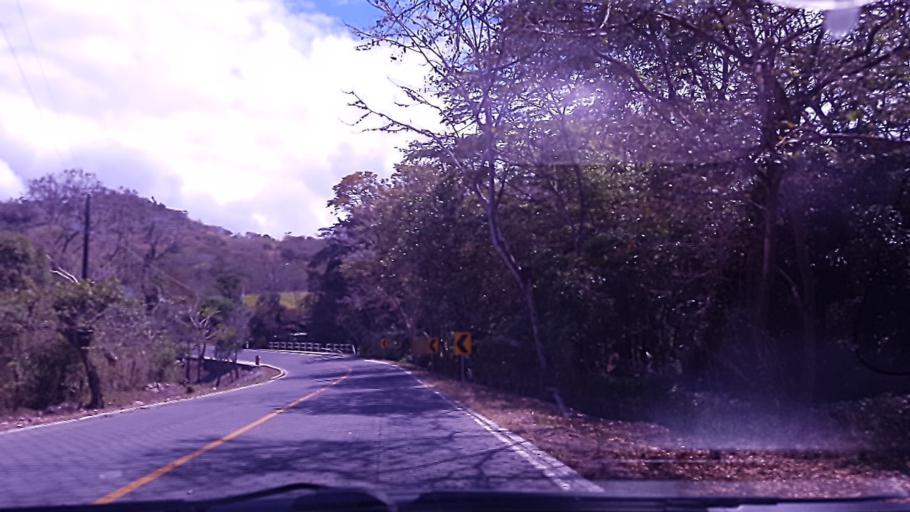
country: NI
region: Esteli
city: Condega
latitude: 13.4053
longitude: -86.2939
